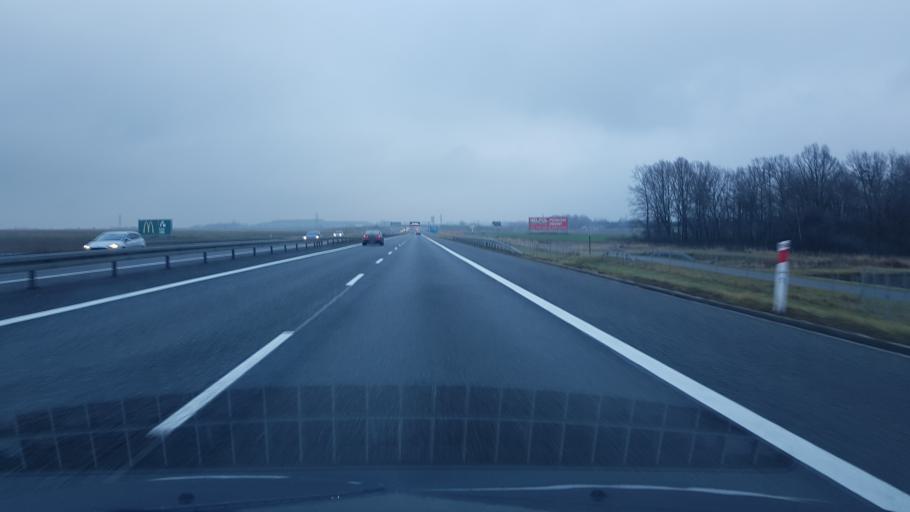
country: PL
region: Silesian Voivodeship
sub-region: Powiat gliwicki
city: Zernica
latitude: 50.2623
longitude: 18.6283
